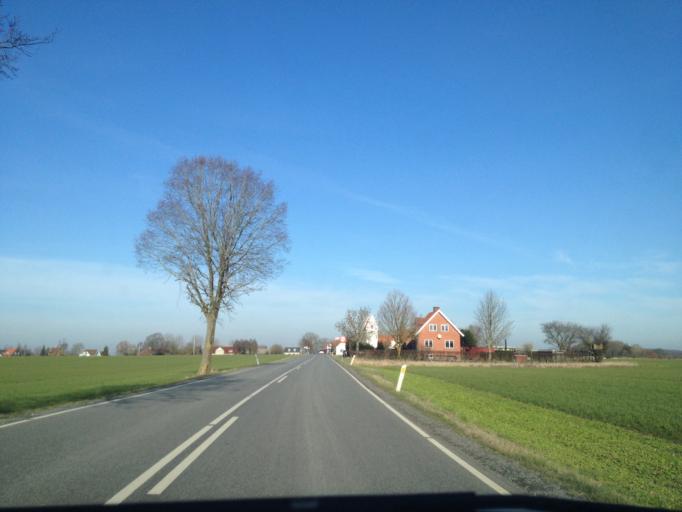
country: DK
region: South Denmark
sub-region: Kerteminde Kommune
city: Kerteminde
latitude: 55.4132
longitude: 10.6601
